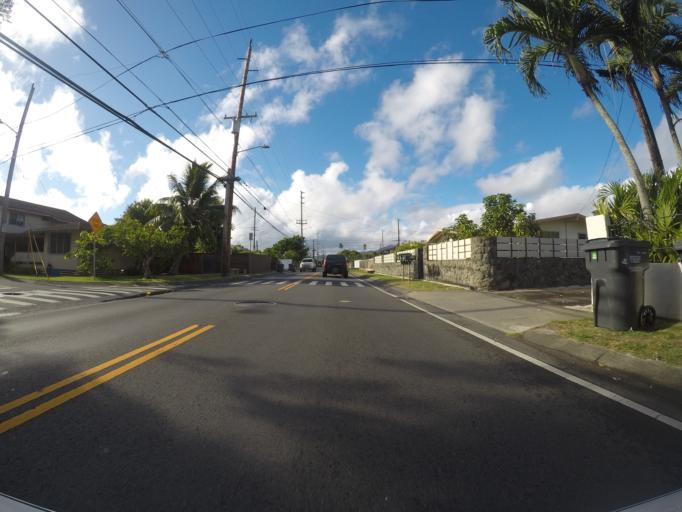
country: US
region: Hawaii
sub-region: Honolulu County
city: Kailua
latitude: 21.4067
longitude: -157.7517
